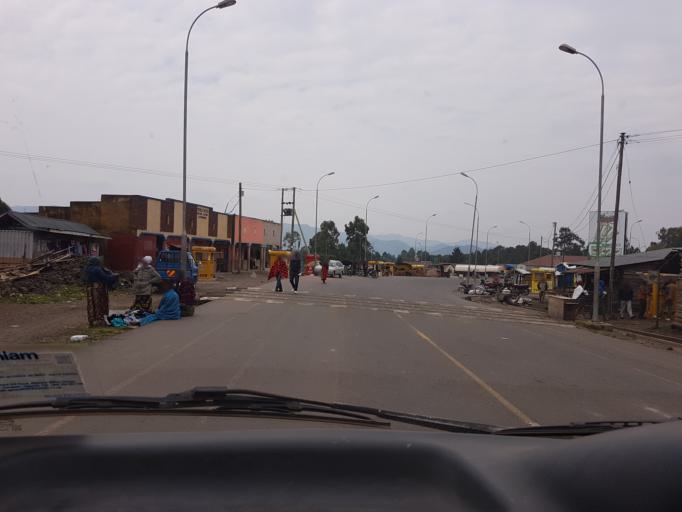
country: UG
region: Western Region
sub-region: Kisoro District
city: Kisoro
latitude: -1.3394
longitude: 29.7394
